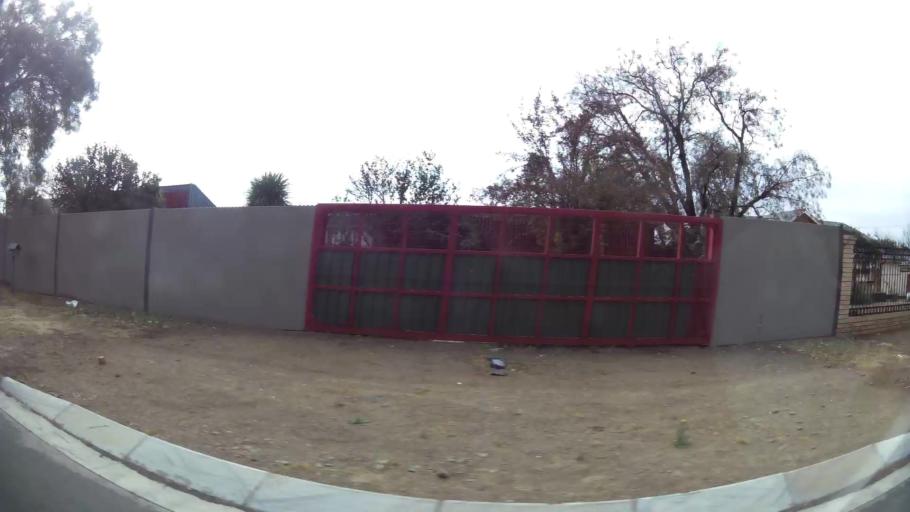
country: ZA
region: Orange Free State
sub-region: Mangaung Metropolitan Municipality
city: Bloemfontein
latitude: -29.0895
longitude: 26.2366
